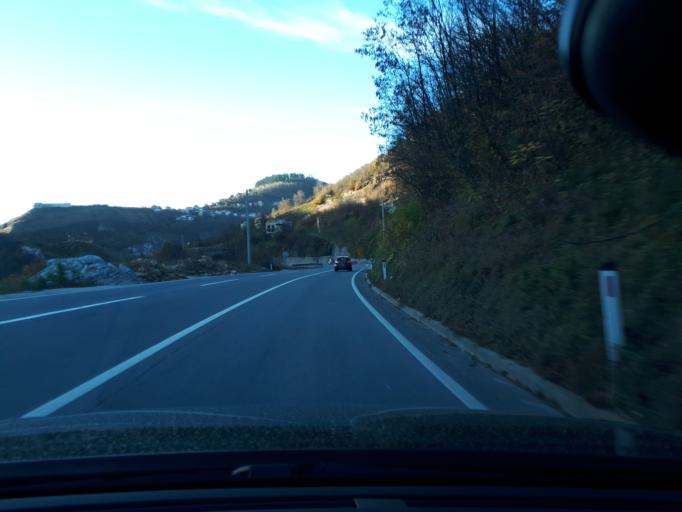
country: BA
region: Federation of Bosnia and Herzegovina
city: Kobilja Glava
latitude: 43.8545
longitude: 18.4591
